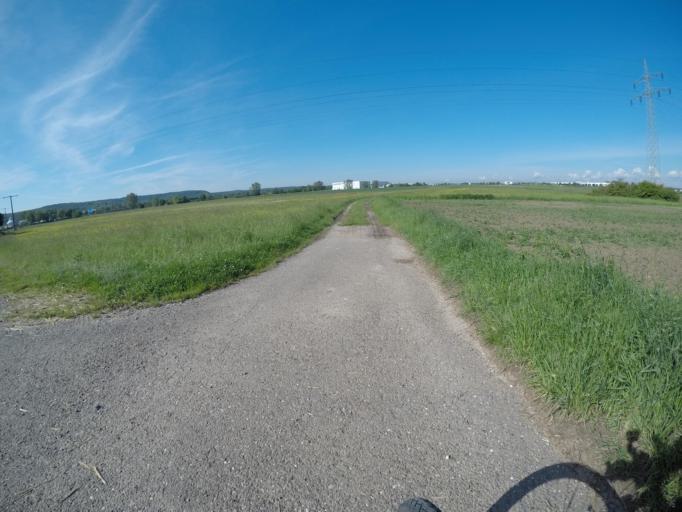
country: DE
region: Baden-Wuerttemberg
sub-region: Regierungsbezirk Stuttgart
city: Ehningen
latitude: 48.6449
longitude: 8.9273
